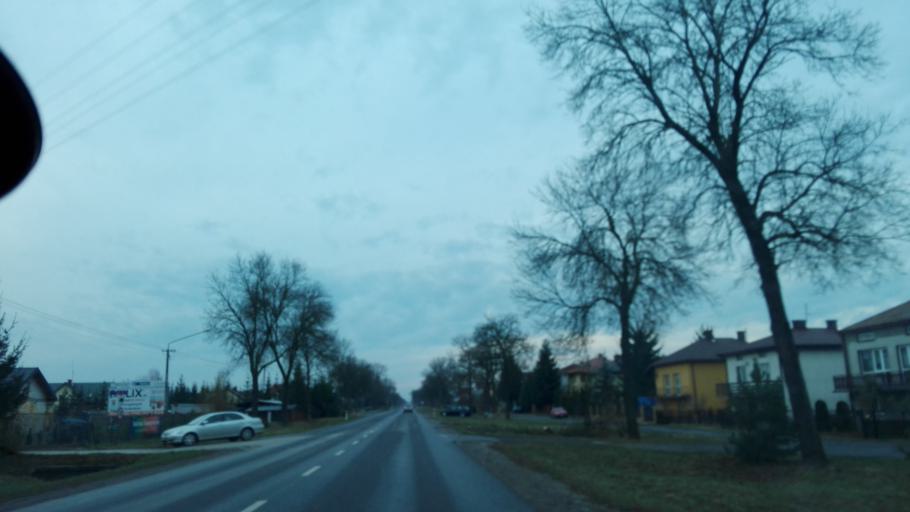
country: PL
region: Lublin Voivodeship
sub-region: Powiat radzynski
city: Radzyn Podlaski
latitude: 51.7751
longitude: 22.6391
